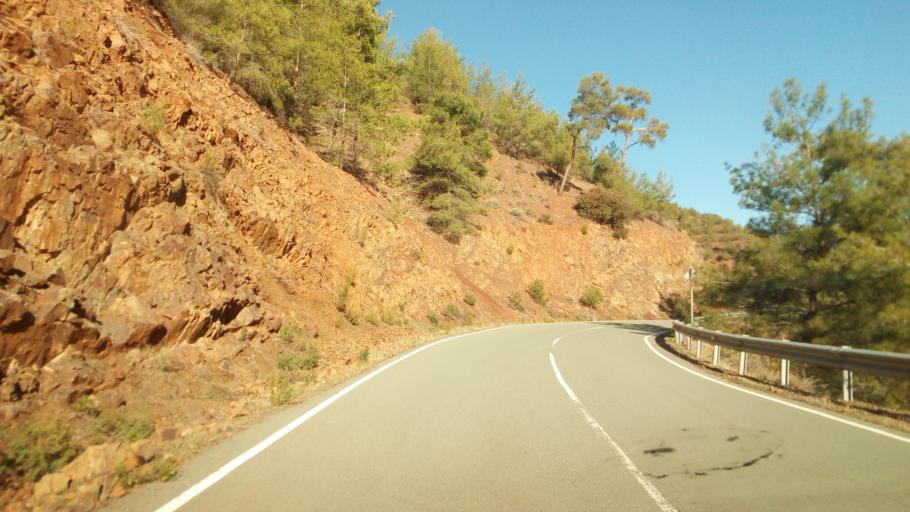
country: CY
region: Lefkosia
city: Lefka
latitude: 35.0952
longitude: 32.7579
